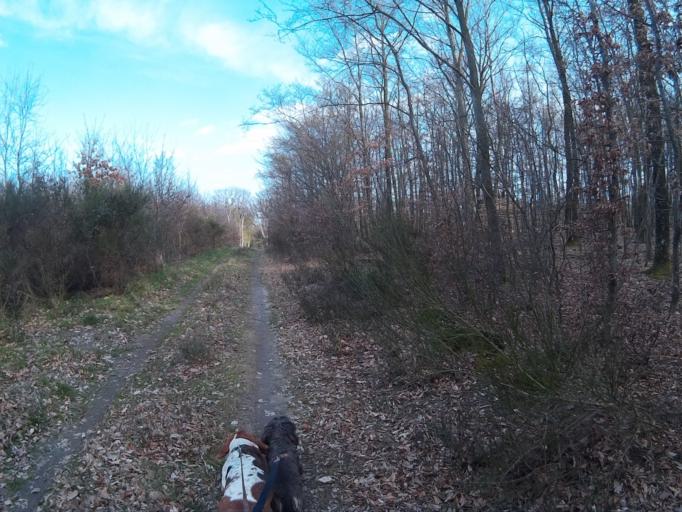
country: HU
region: Vas
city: Sarvar
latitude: 47.1946
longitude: 16.9941
